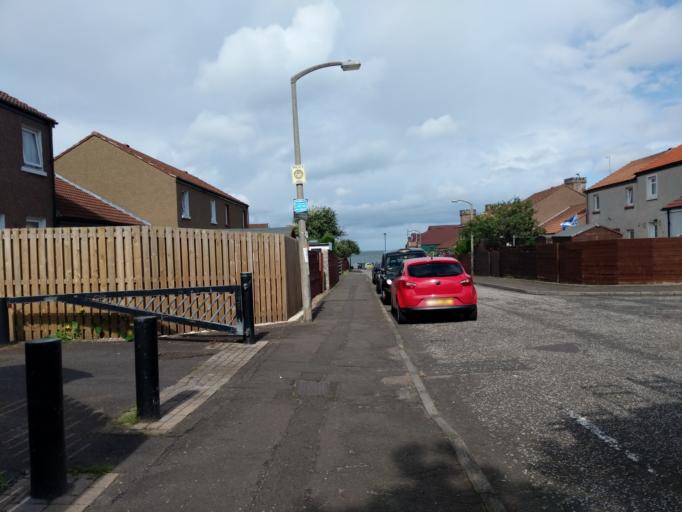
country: GB
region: Scotland
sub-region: West Lothian
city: Seafield
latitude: 55.9551
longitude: -3.1144
